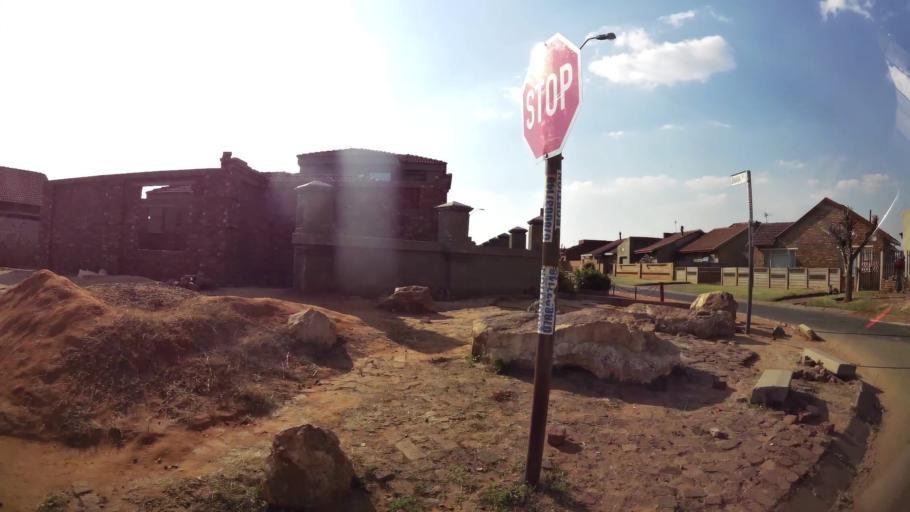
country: ZA
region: Gauteng
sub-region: Ekurhuleni Metropolitan Municipality
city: Benoni
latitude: -26.1534
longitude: 28.4020
